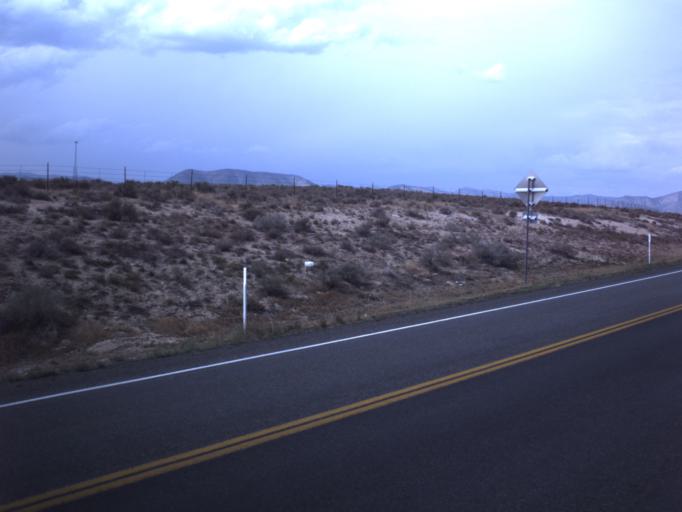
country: US
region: Utah
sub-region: Sanpete County
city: Gunnison
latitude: 39.1670
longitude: -111.8201
